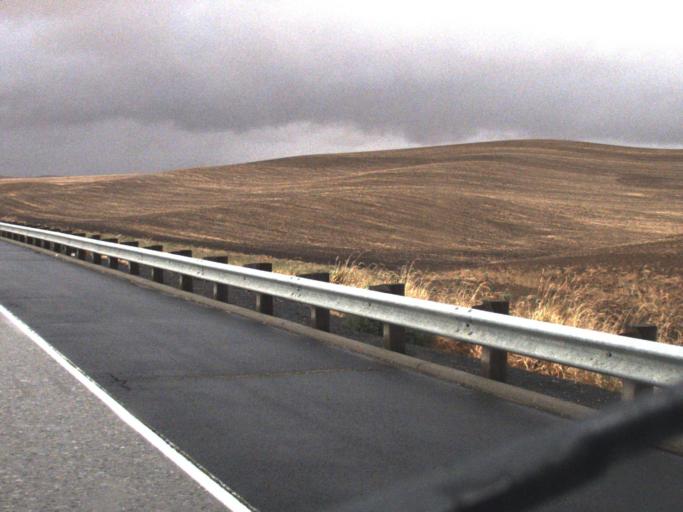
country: US
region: Washington
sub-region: Whitman County
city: Colfax
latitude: 47.0345
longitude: -117.3662
